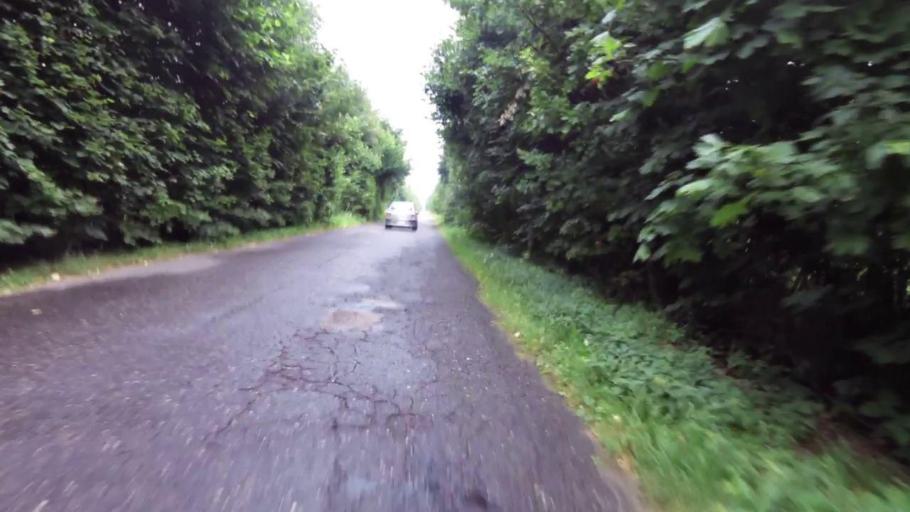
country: PL
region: West Pomeranian Voivodeship
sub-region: Powiat stargardzki
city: Insko
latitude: 53.4816
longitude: 15.6104
